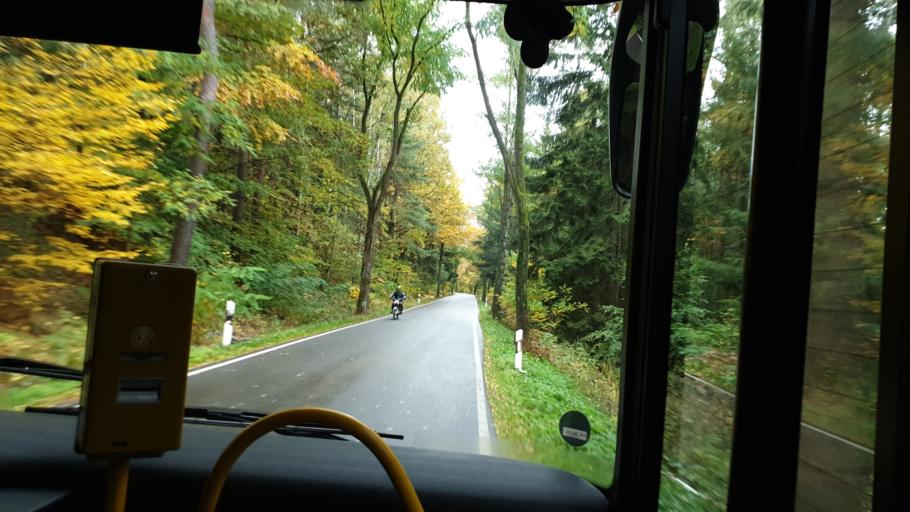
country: DE
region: Saxony
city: Kurort Gohrisch
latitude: 50.8893
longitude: 14.1049
